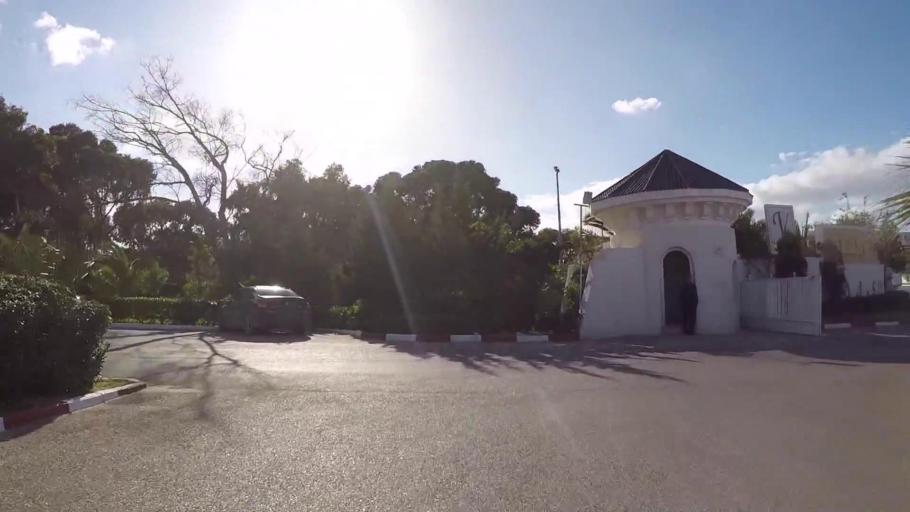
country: TN
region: Nabul
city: Al Hammamat
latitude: 36.3597
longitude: 10.5309
